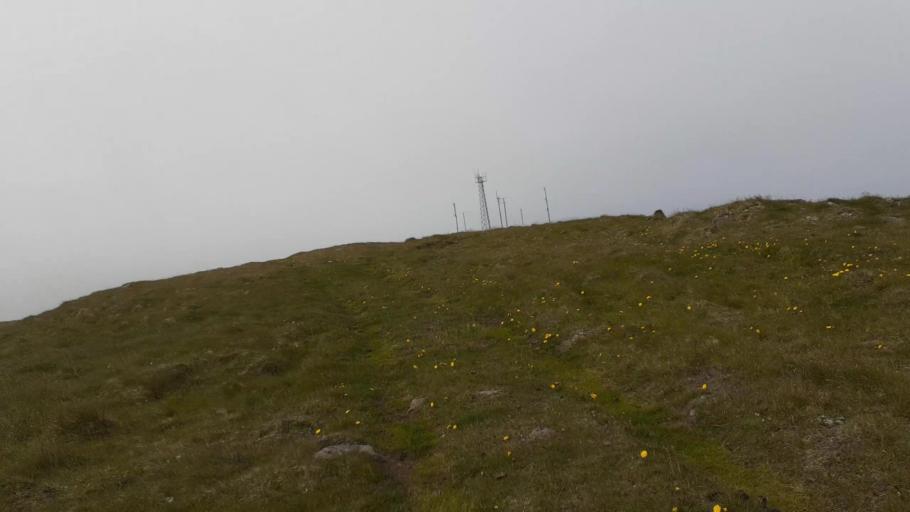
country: IS
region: Northeast
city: Dalvik
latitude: 66.5438
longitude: -17.9925
